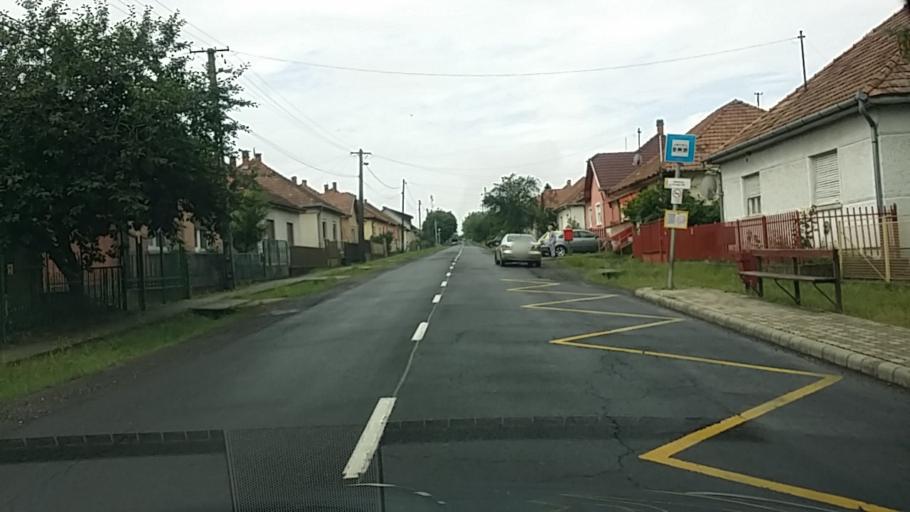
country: SK
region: Nitriansky
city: Sahy
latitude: 48.0157
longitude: 18.8879
